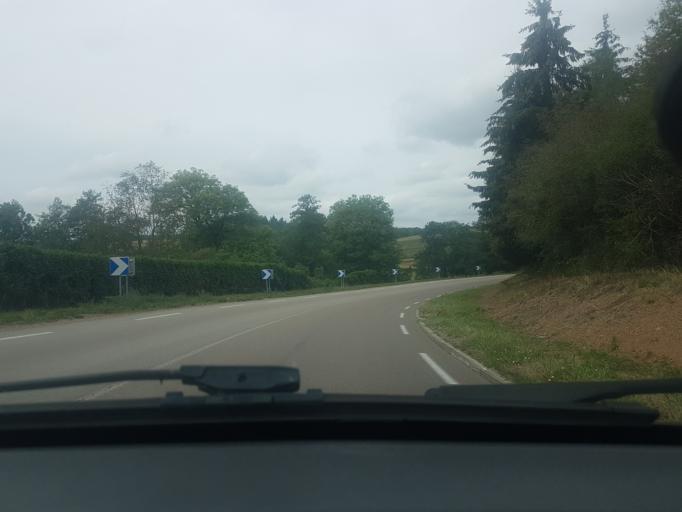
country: FR
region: Bourgogne
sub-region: Departement de la Cote-d'Or
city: Arnay-le-Duc
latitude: 47.1401
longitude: 4.4556
